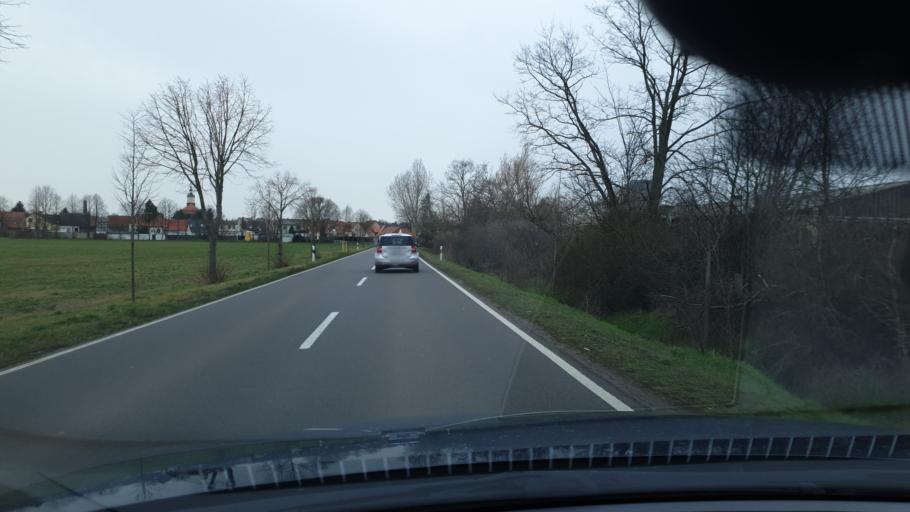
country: DE
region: Saxony-Anhalt
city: Oranienbaum
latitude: 51.7955
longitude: 12.4146
